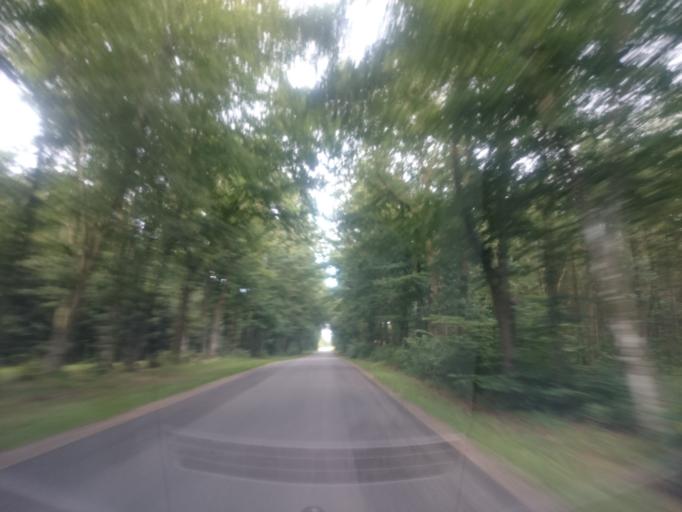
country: DK
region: South Denmark
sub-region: Billund Kommune
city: Grindsted
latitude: 55.6467
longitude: 8.8549
